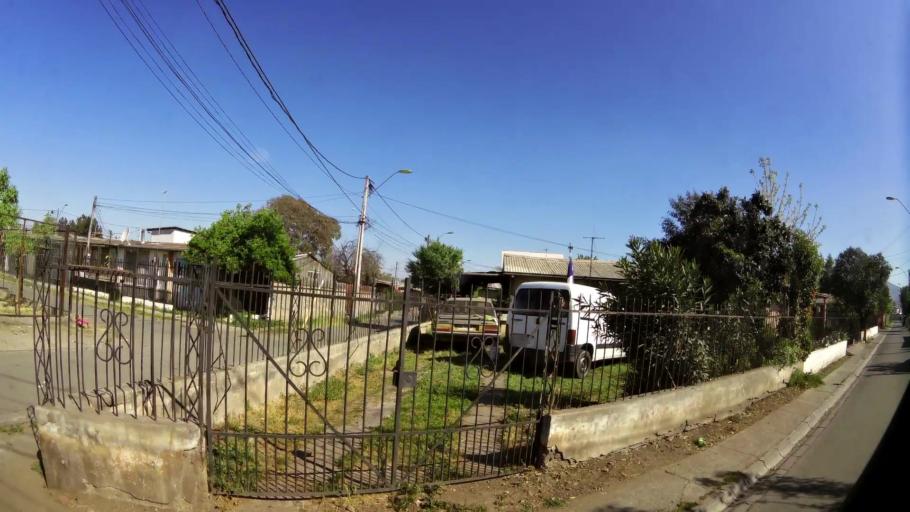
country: CL
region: Santiago Metropolitan
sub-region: Provincia de Talagante
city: Penaflor
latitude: -33.6068
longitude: -70.8917
